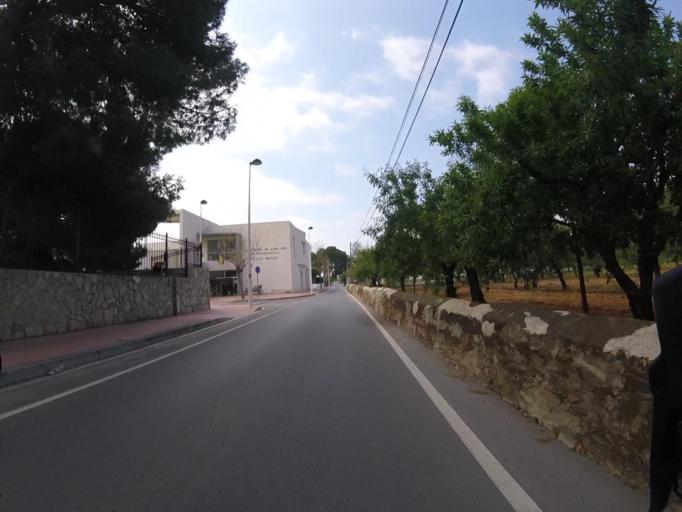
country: ES
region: Valencia
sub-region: Provincia de Castello
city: Alcoceber
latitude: 40.2433
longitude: 0.2725
